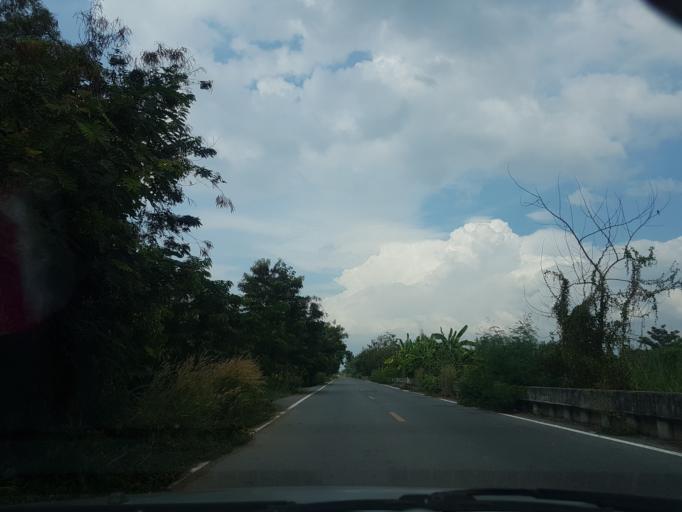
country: TH
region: Sara Buri
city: Nong Khae
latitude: 14.2560
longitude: 100.8913
